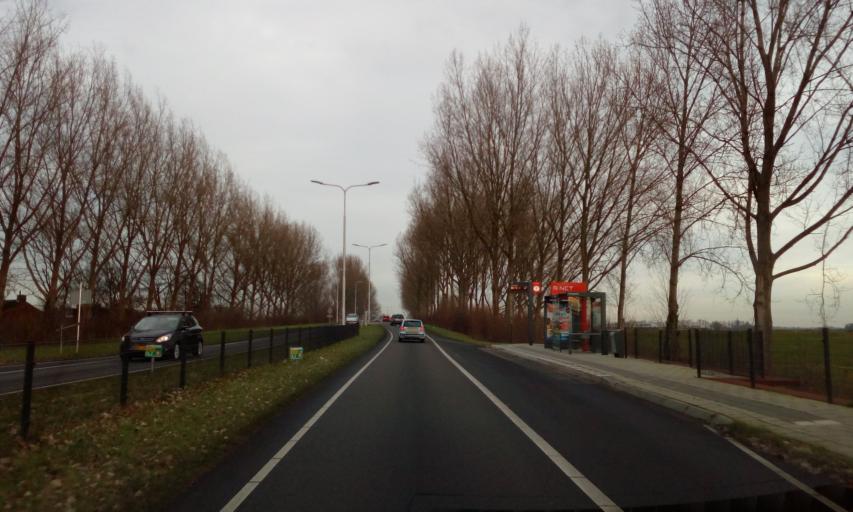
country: NL
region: South Holland
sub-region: Gemeente Zoetermeer
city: Zoetermeer
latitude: 52.0928
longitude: 4.4742
